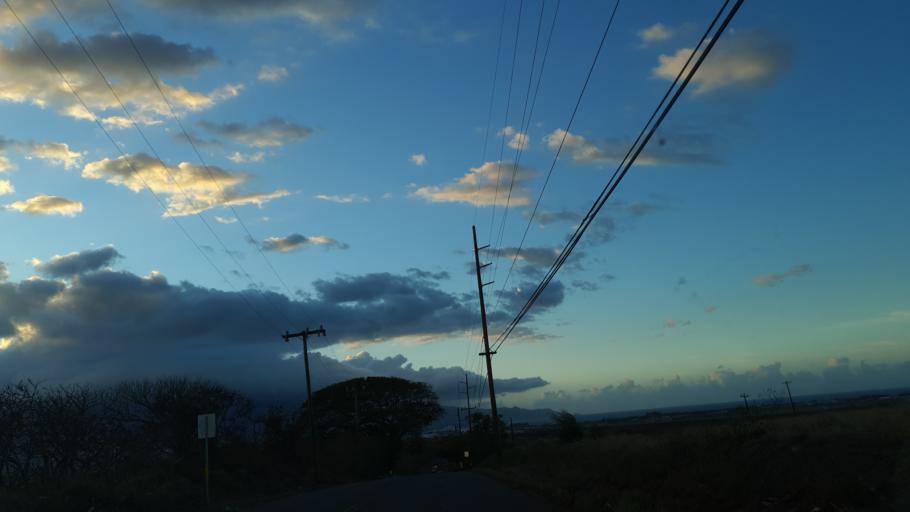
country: US
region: Hawaii
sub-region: Maui County
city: Kahului
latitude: 20.8644
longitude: -156.4307
